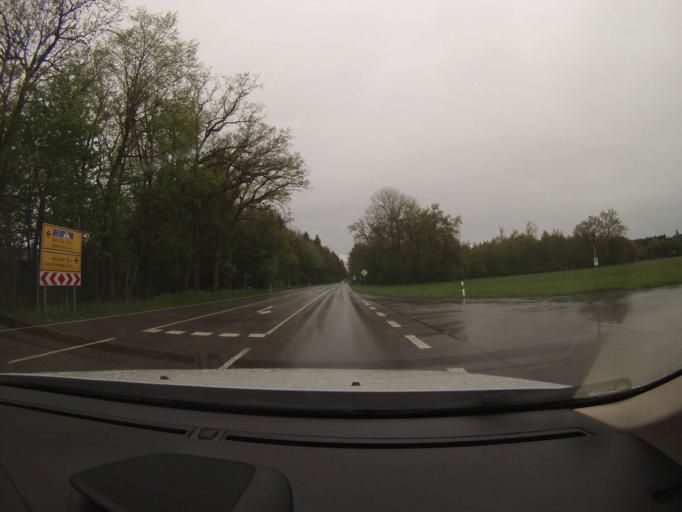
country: DE
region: Bavaria
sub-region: Upper Bavaria
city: Sauerlach
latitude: 47.9966
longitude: 11.6416
